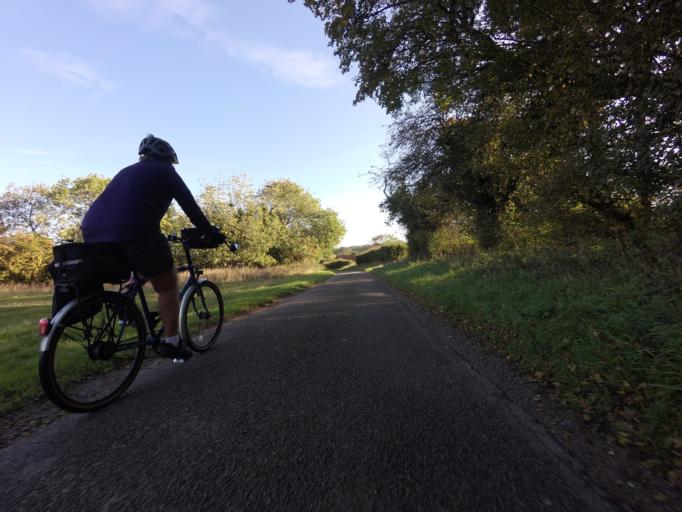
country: GB
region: England
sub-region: Norfolk
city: Dersingham
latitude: 52.8303
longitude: 0.5640
